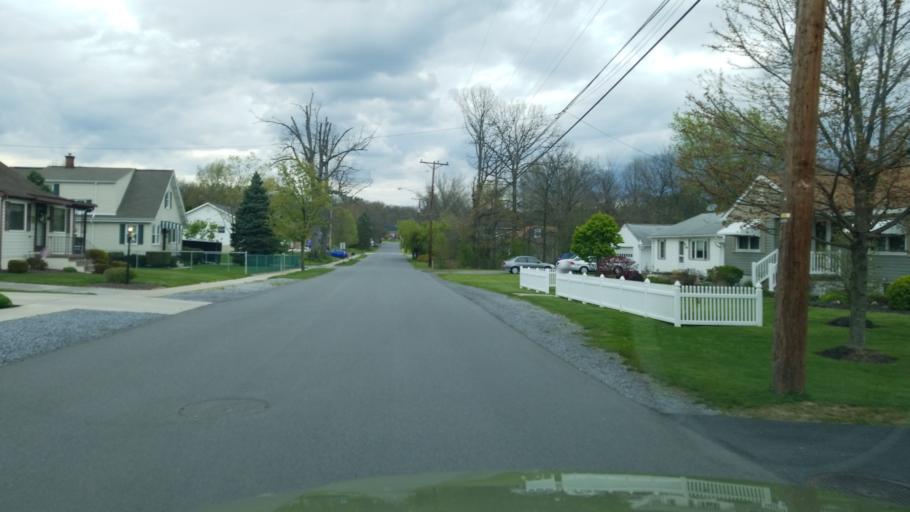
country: US
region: Pennsylvania
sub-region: Blair County
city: Hollidaysburg
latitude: 40.4369
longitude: -78.3993
